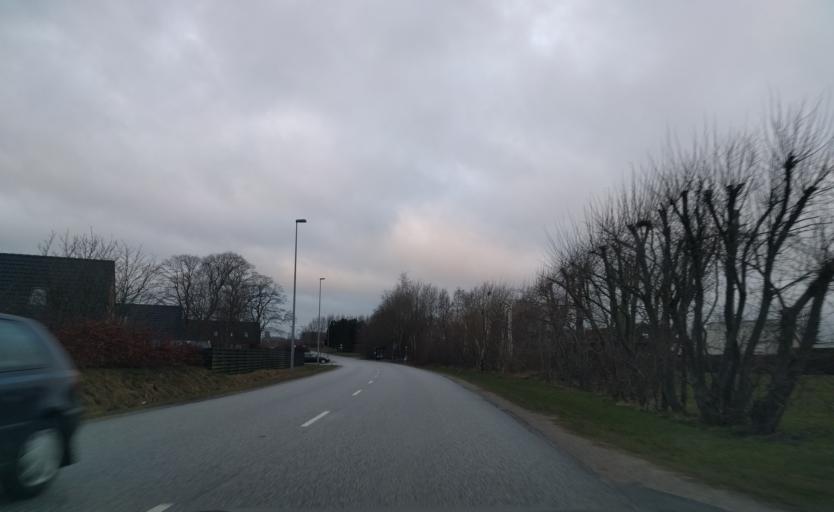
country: DK
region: North Denmark
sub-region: Alborg Kommune
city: Gistrup
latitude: 57.0120
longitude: 9.9818
